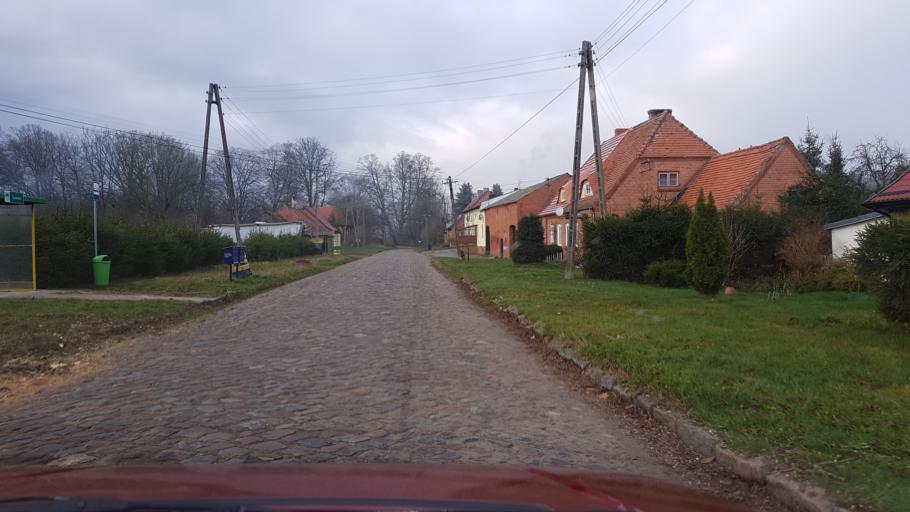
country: PL
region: West Pomeranian Voivodeship
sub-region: Powiat bialogardzki
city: Tychowo
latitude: 53.9793
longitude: 16.3146
